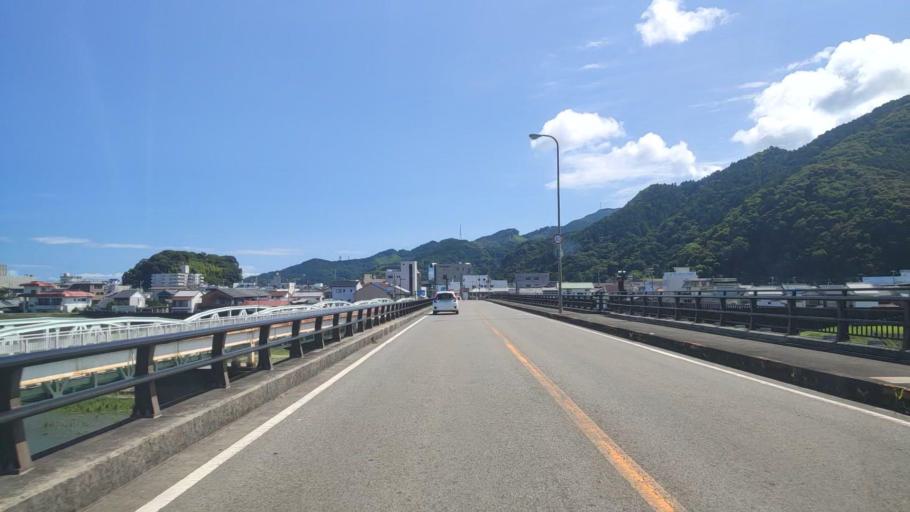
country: JP
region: Wakayama
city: Shingu
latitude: 33.7330
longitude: 135.9875
